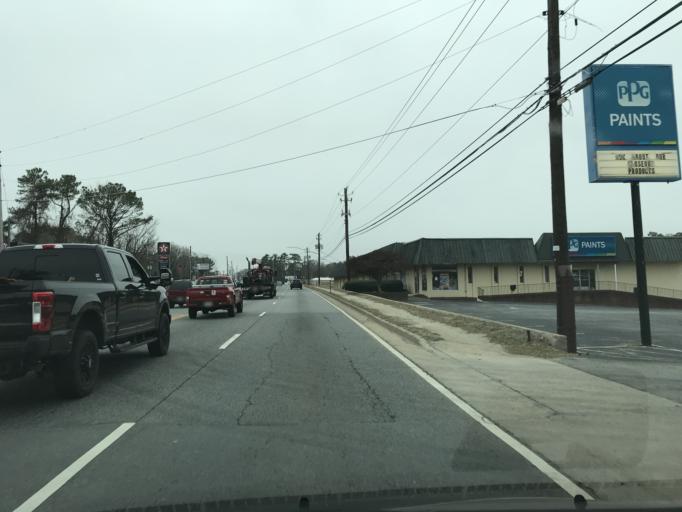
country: US
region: Georgia
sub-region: DeKalb County
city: Tucker
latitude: 33.8463
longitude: -84.2292
